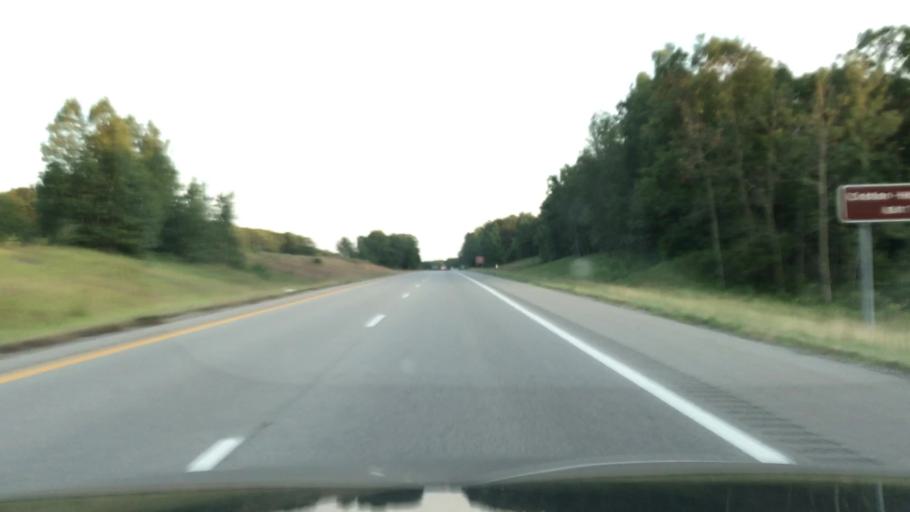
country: US
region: Michigan
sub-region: Montcalm County
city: Howard City
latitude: 43.5041
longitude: -85.4867
